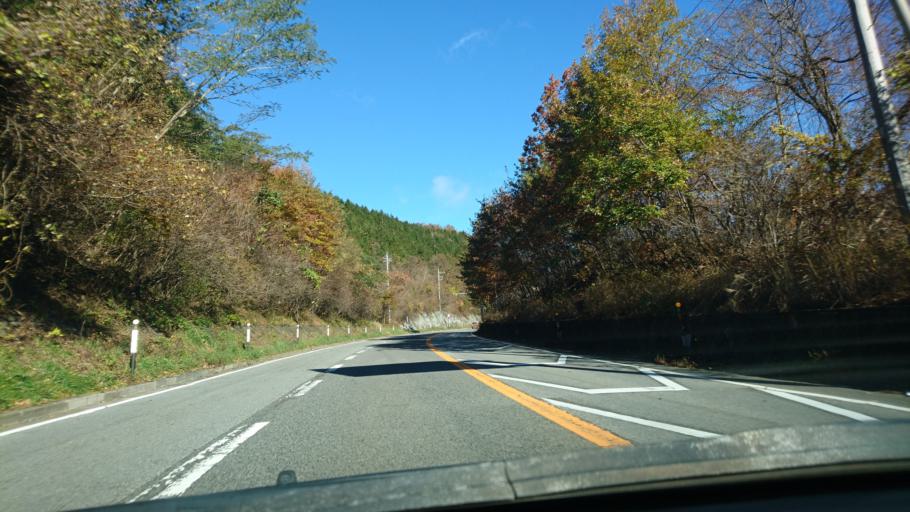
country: JP
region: Nagano
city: Saku
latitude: 36.3151
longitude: 138.6502
